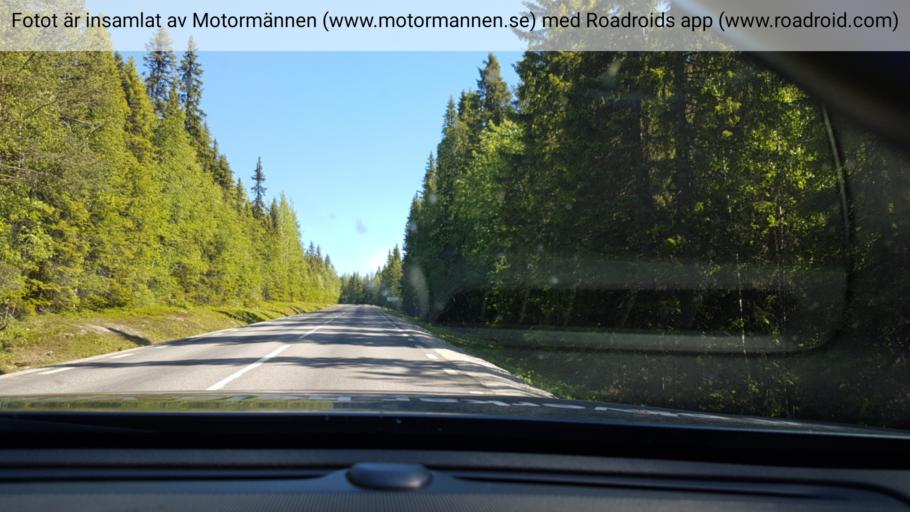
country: SE
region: Vaesterbotten
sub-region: Asele Kommun
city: Insjon
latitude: 64.7187
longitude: 17.6667
